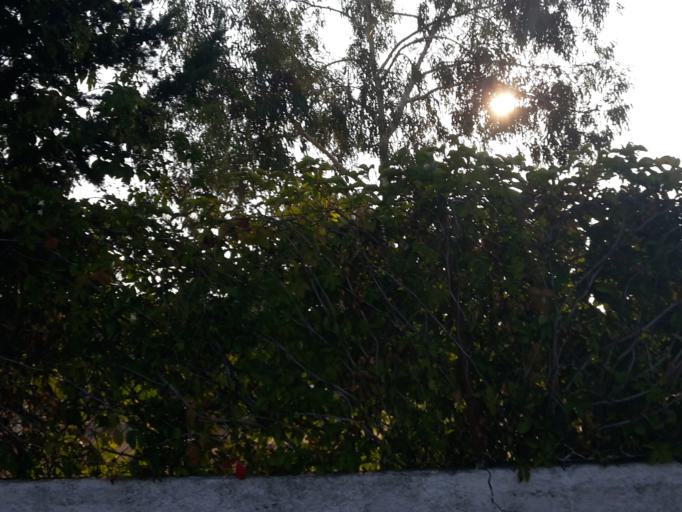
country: TR
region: Antalya
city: Kemer
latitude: 36.6043
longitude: 30.5594
